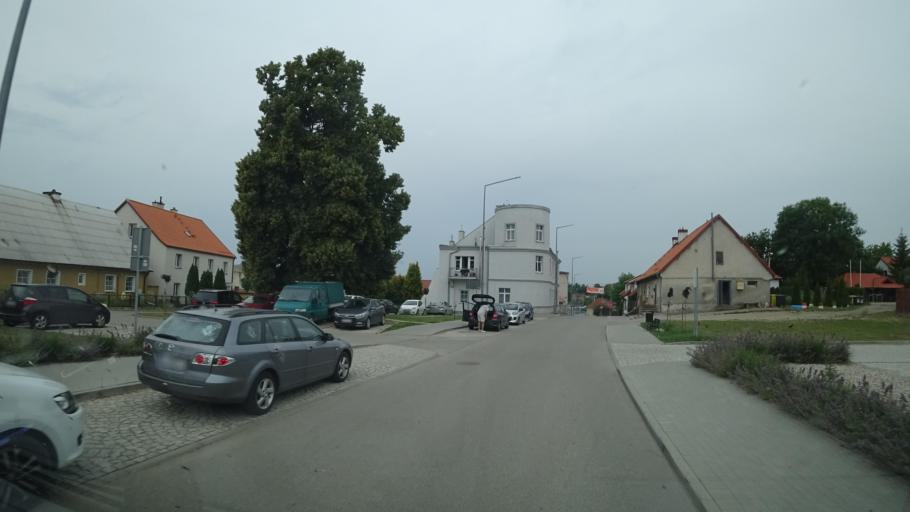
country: PL
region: Warmian-Masurian Voivodeship
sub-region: Powiat gizycki
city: Ryn
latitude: 53.9372
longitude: 21.5487
